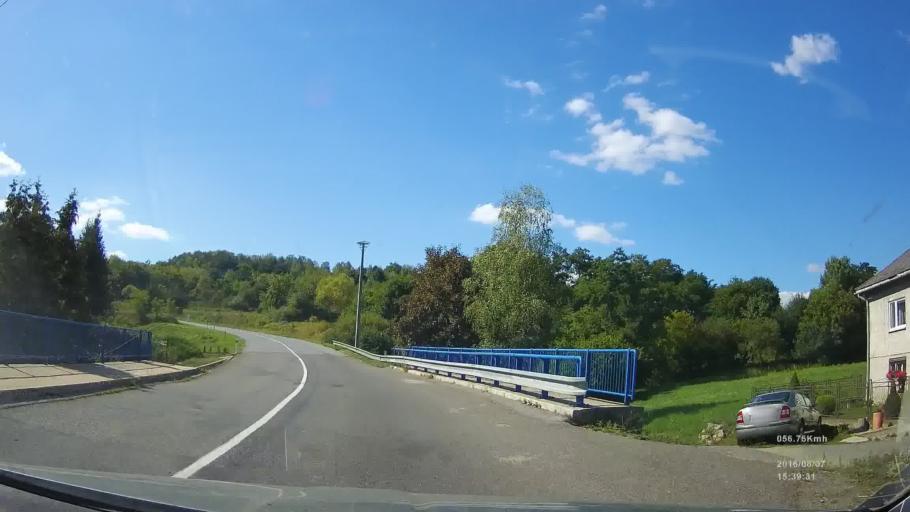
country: SK
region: Presovsky
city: Giraltovce
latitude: 49.1187
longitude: 21.6033
